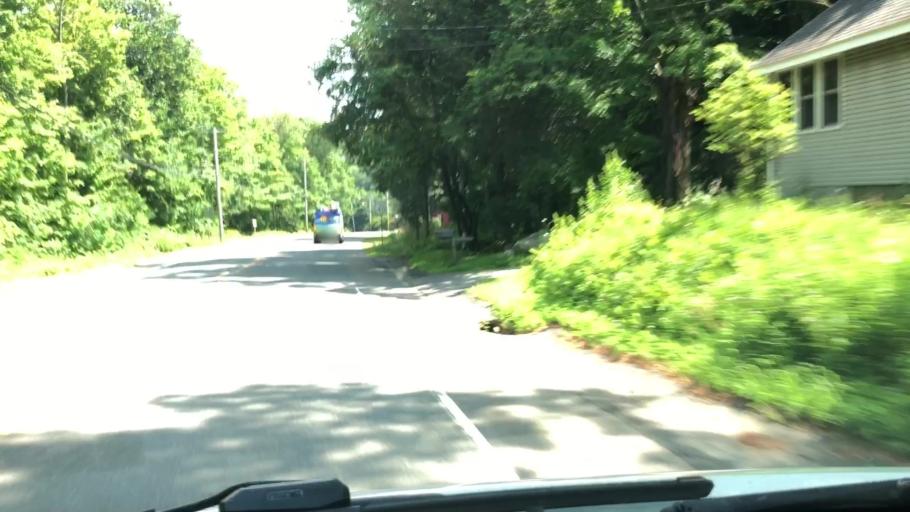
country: US
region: Massachusetts
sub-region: Hampshire County
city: Williamsburg
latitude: 42.3982
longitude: -72.7424
